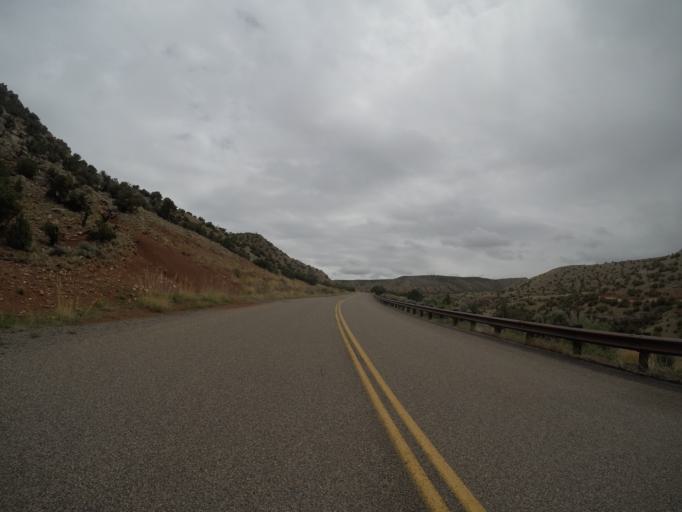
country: US
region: Wyoming
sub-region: Big Horn County
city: Lovell
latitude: 45.1009
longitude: -108.2190
